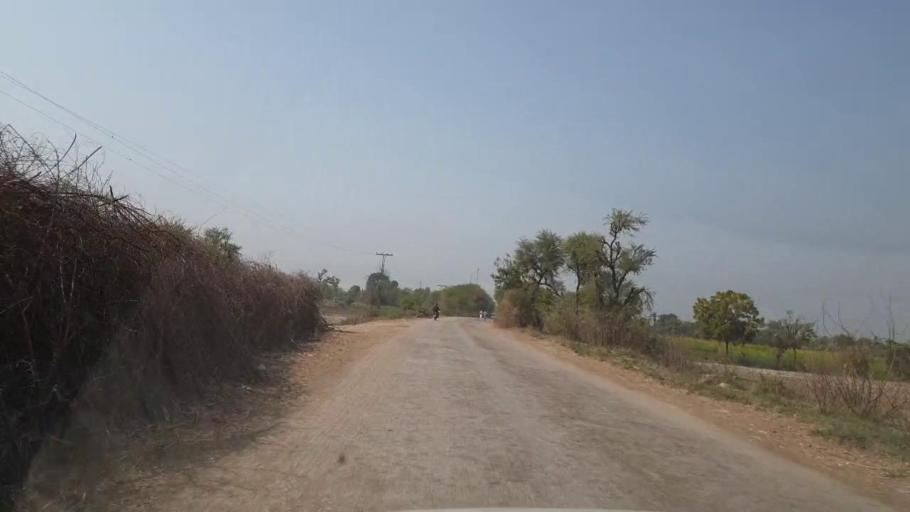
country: PK
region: Sindh
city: Mirpur Khas
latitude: 25.7032
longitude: 69.1369
